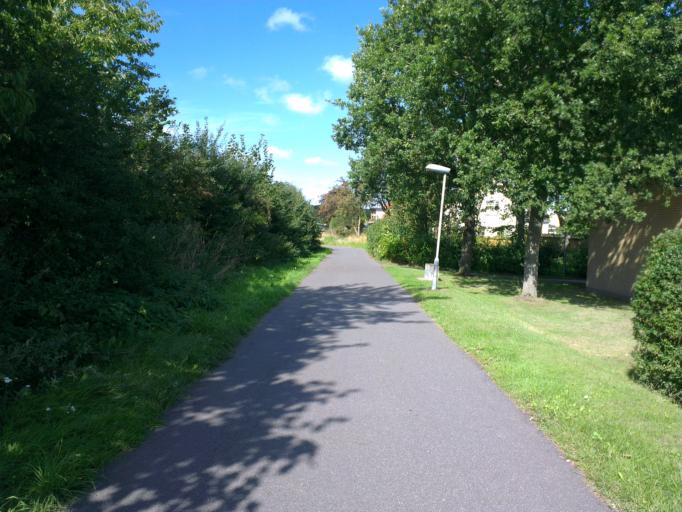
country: DK
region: Capital Region
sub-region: Frederikssund Kommune
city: Jaegerspris
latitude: 55.8521
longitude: 11.9836
